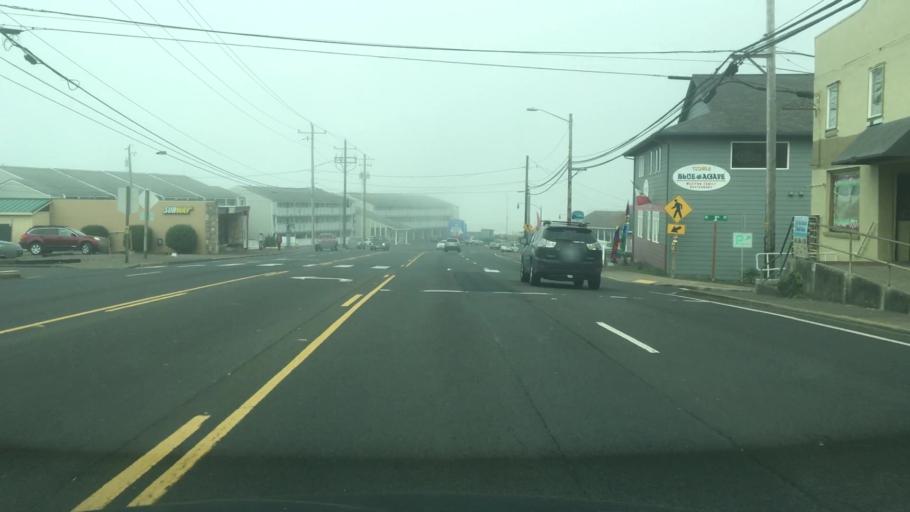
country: US
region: Oregon
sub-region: Lincoln County
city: Lincoln City
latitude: 44.9647
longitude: -124.0177
